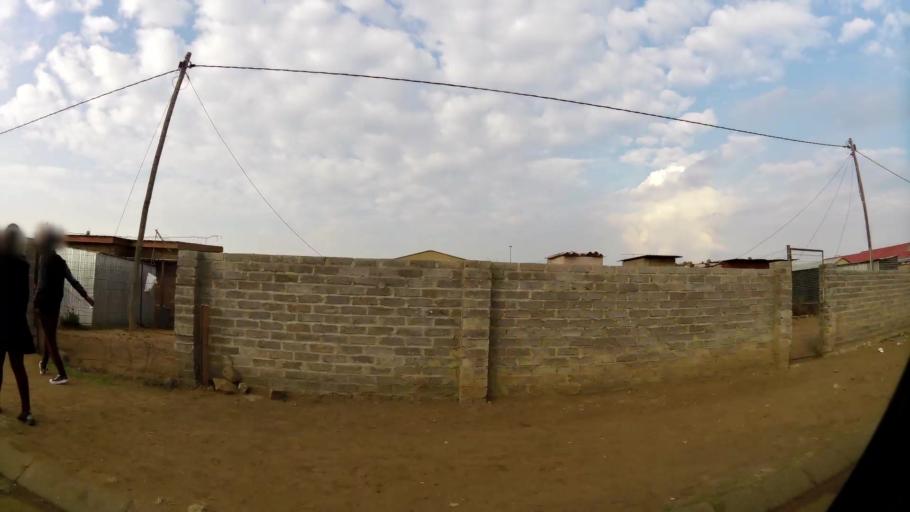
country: ZA
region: Gauteng
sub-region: Sedibeng District Municipality
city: Vanderbijlpark
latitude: -26.6764
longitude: 27.8688
